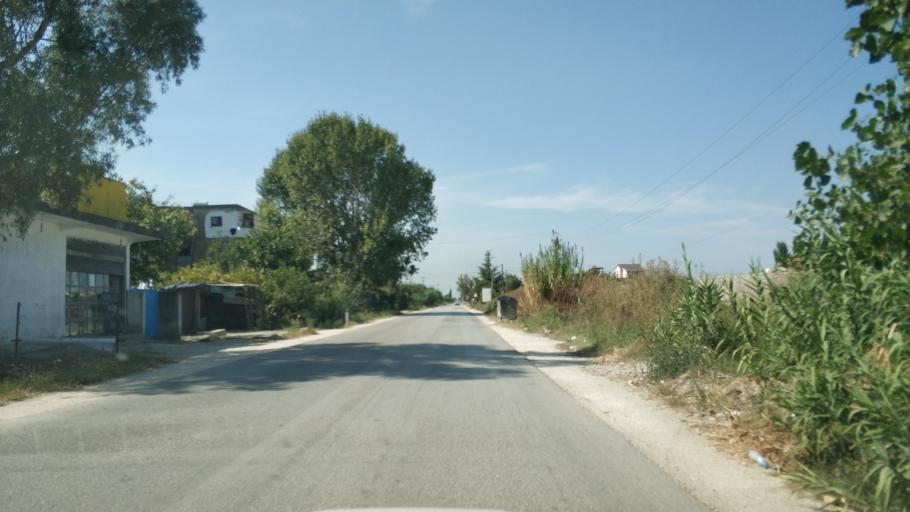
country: AL
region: Fier
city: Fier
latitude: 40.7291
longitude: 19.5453
